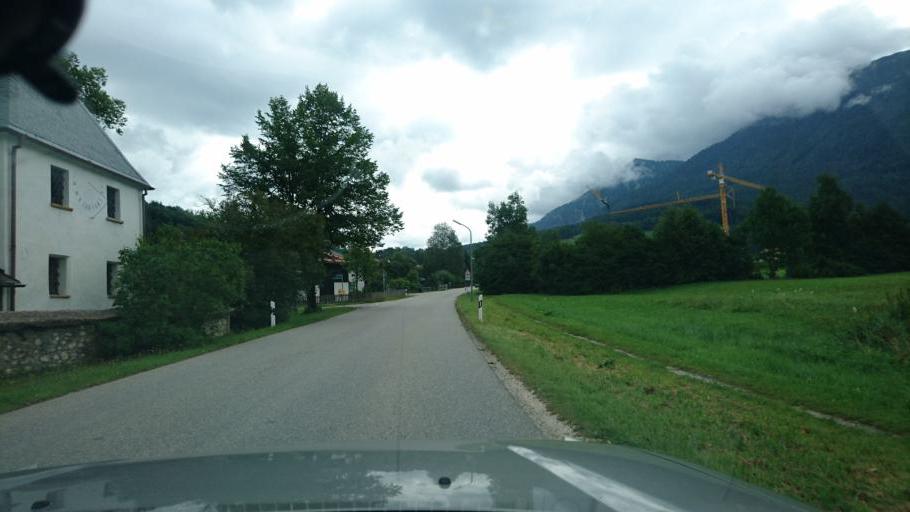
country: DE
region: Bavaria
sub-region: Upper Bavaria
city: Ruhpolding
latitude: 47.7565
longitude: 12.6626
